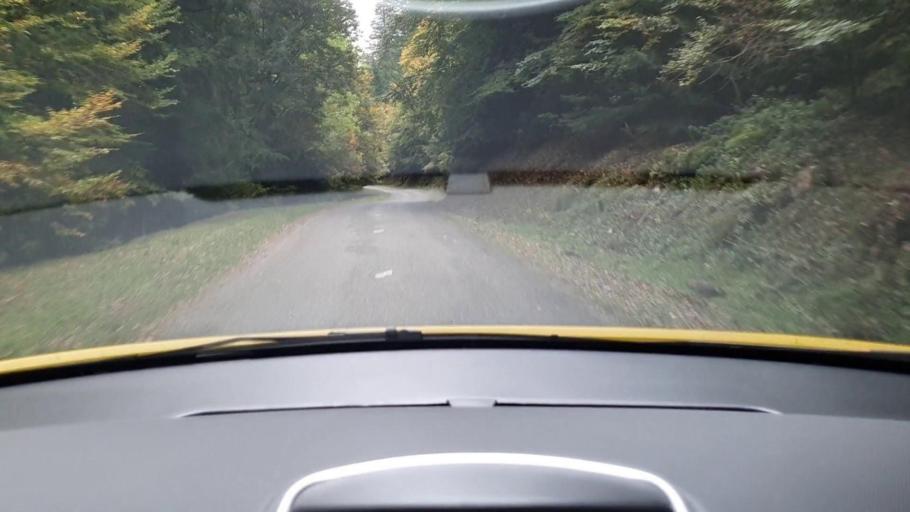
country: FR
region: Languedoc-Roussillon
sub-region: Departement de la Lozere
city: Meyrueis
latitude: 44.0890
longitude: 3.4493
